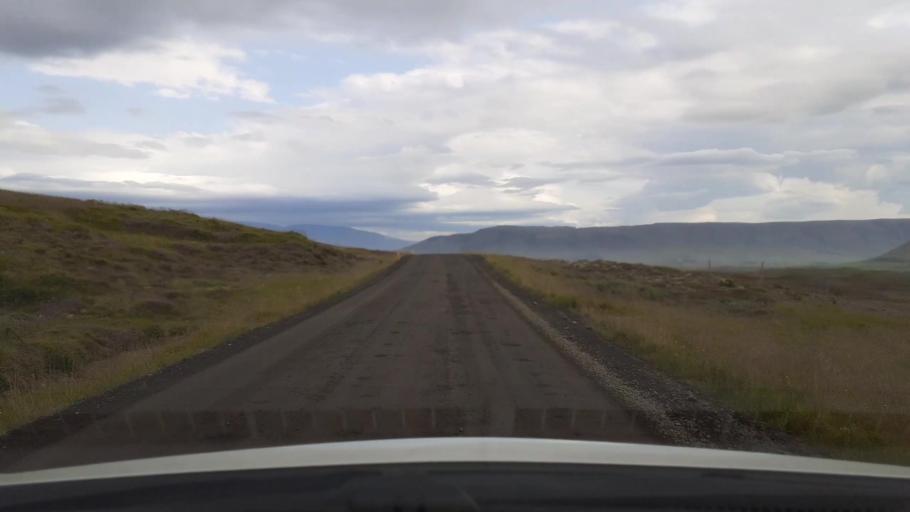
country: IS
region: Capital Region
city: Mosfellsbaer
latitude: 64.2997
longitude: -21.6606
